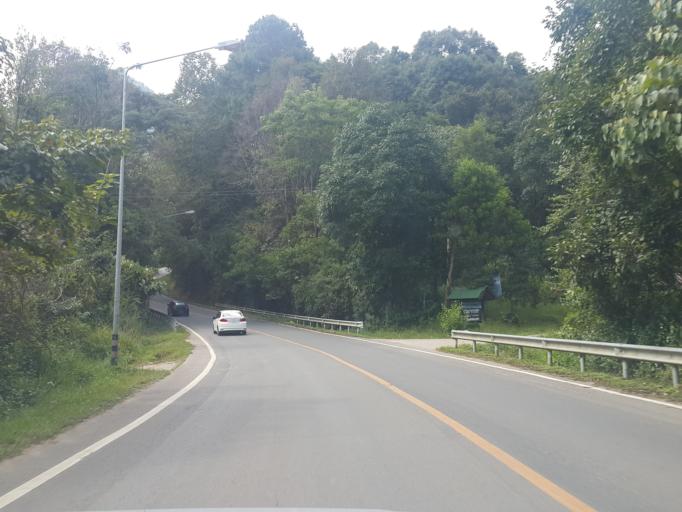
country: TH
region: Chiang Mai
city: Chom Thong
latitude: 18.5479
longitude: 98.5441
